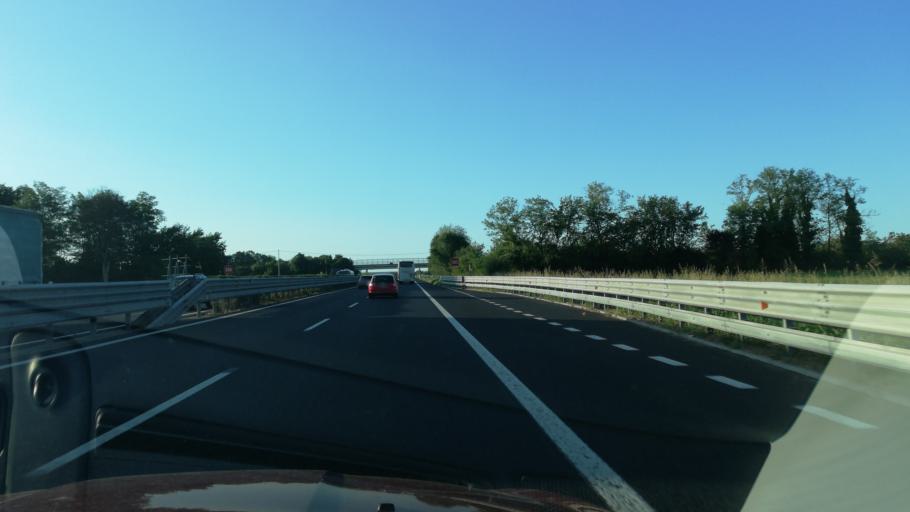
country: IT
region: Friuli Venezia Giulia
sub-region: Provincia di Udine
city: Zugliano-Terenzano-Cargnacco
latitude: 45.9899
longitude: 13.2369
